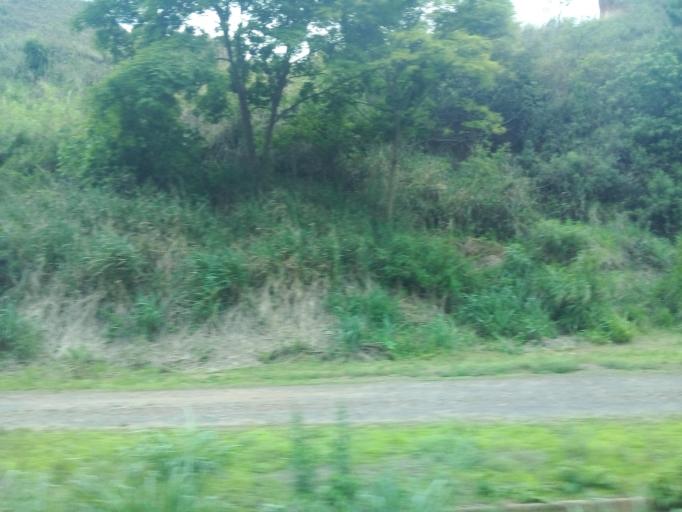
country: BR
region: Minas Gerais
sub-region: Nova Era
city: Nova Era
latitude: -19.7267
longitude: -43.0094
